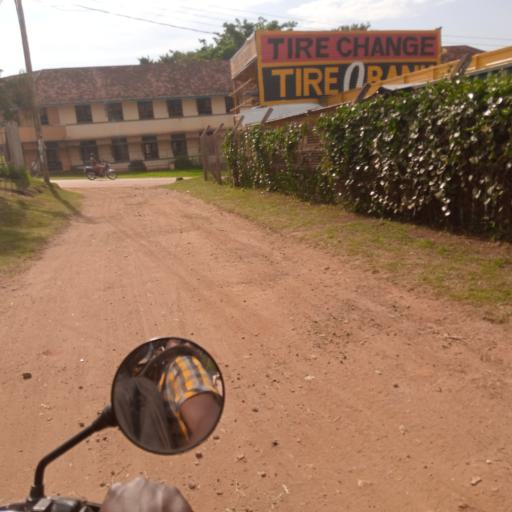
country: UG
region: Eastern Region
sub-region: Mbale District
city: Mbale
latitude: 1.0743
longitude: 34.1797
